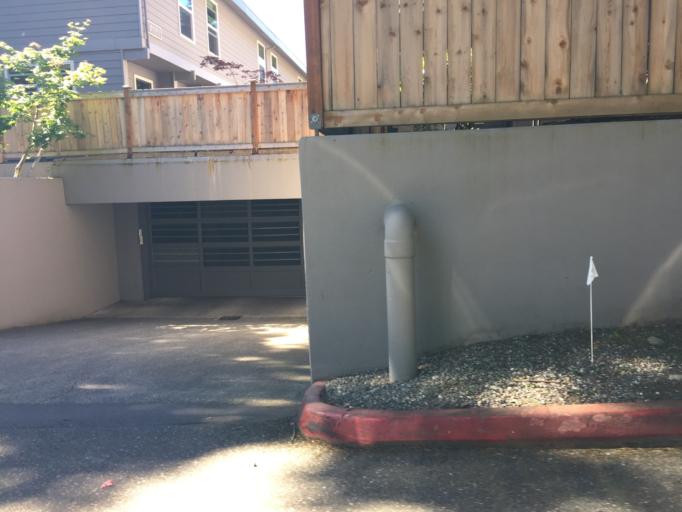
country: US
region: Washington
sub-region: King County
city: Bellevue
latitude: 47.6210
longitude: -122.2061
